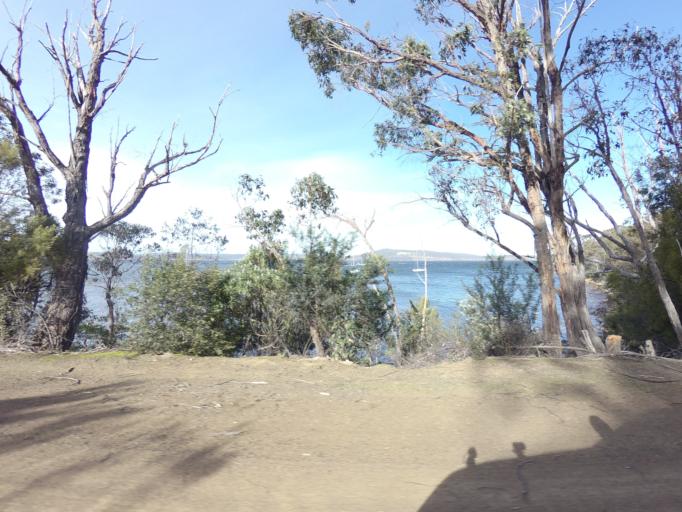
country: AU
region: Tasmania
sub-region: Kingborough
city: Kettering
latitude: -43.1159
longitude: 147.2710
